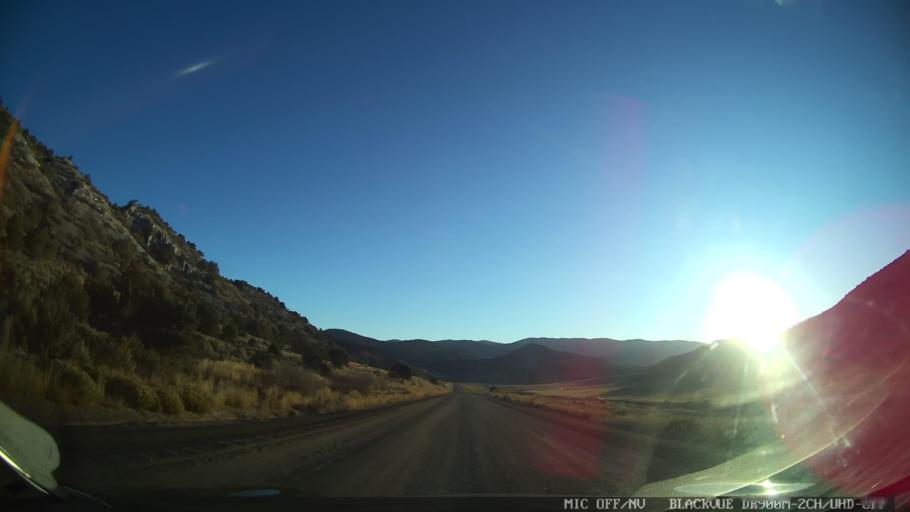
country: US
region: Colorado
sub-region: Grand County
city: Kremmling
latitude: 39.9174
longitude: -106.5491
